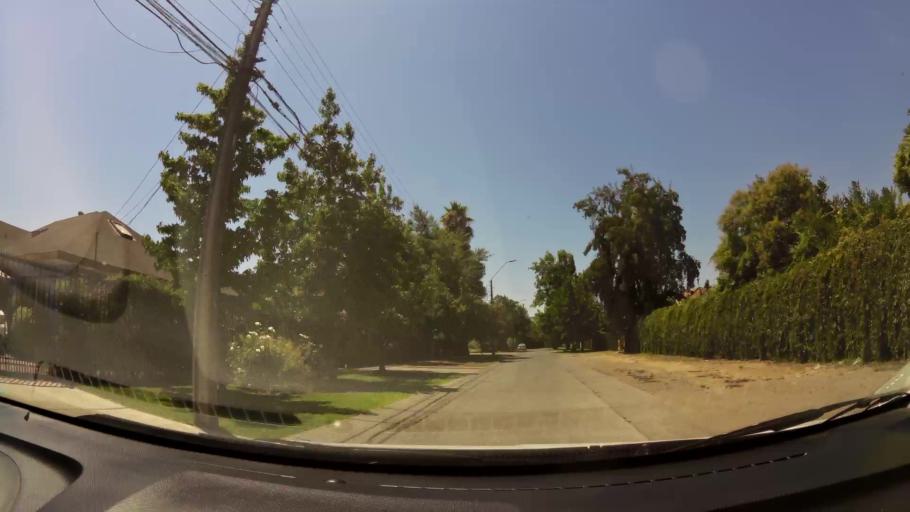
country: CL
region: Maule
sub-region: Provincia de Curico
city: Curico
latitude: -34.9828
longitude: -71.2215
